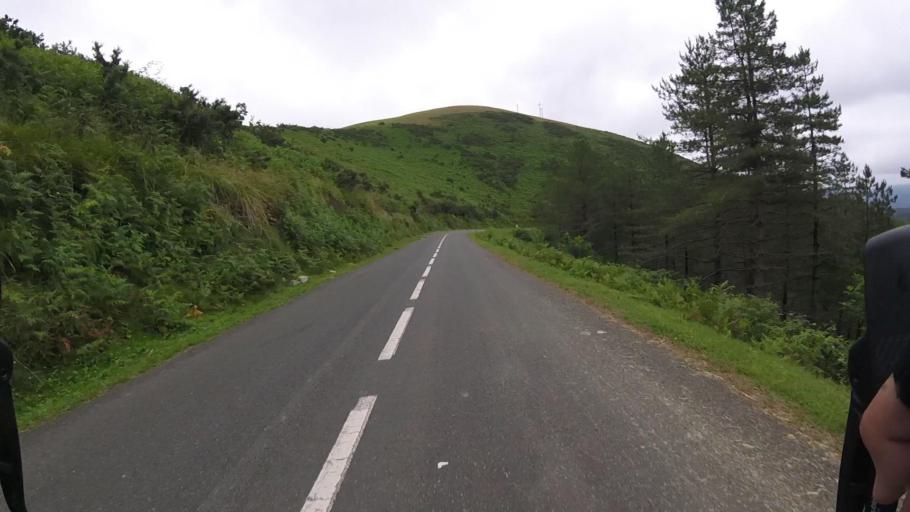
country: ES
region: Navarre
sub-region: Provincia de Navarra
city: Goizueta
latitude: 43.2450
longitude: -1.8117
